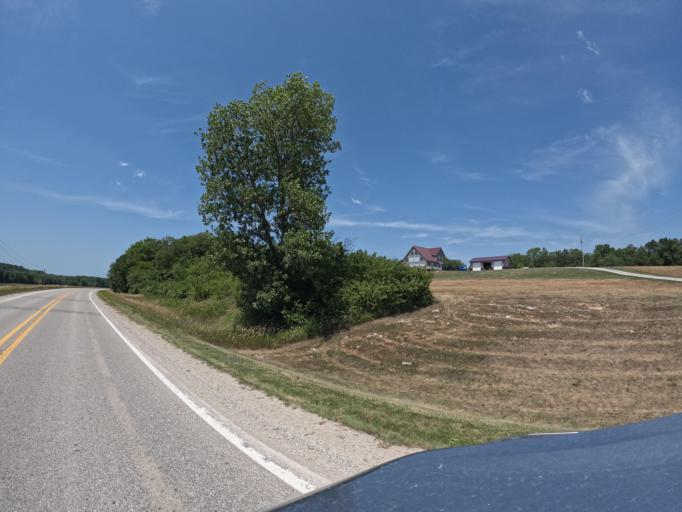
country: US
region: Iowa
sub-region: Henry County
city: Mount Pleasant
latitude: 40.9367
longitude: -91.6041
